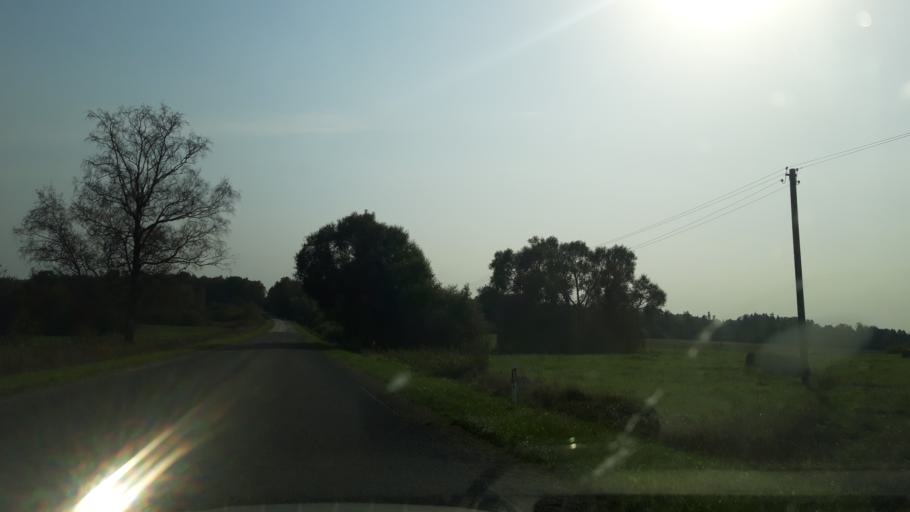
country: LV
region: Burtnieki
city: Matisi
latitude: 57.6576
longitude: 25.2279
